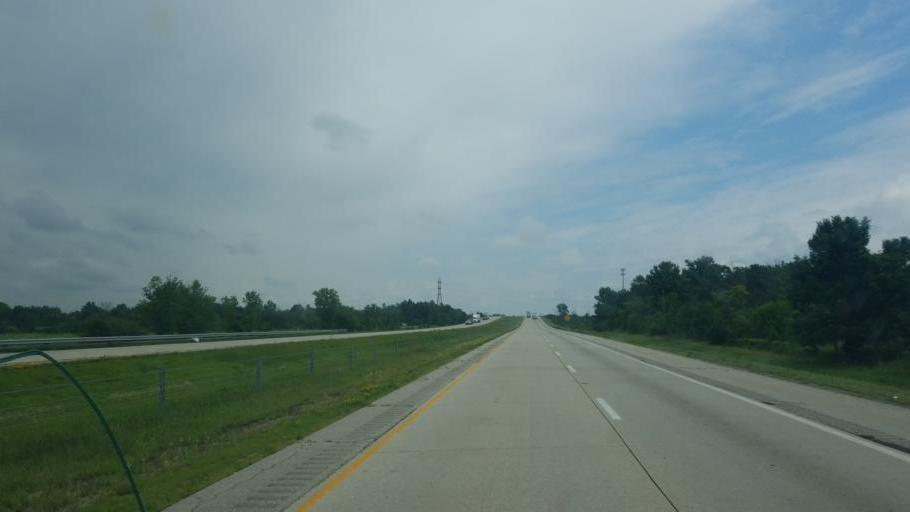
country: US
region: Indiana
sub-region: Huntington County
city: Warren
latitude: 40.6108
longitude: -85.5360
